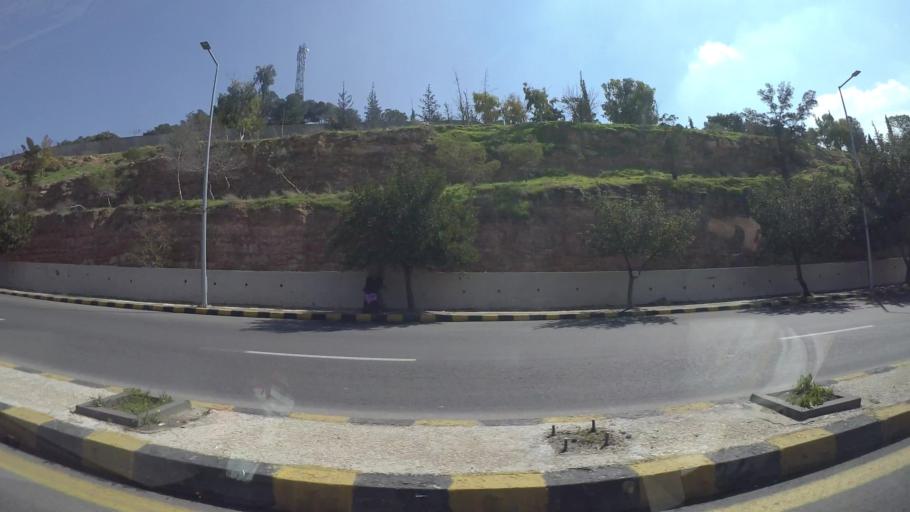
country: JO
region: Amman
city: Amman
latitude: 31.9707
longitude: 35.9727
